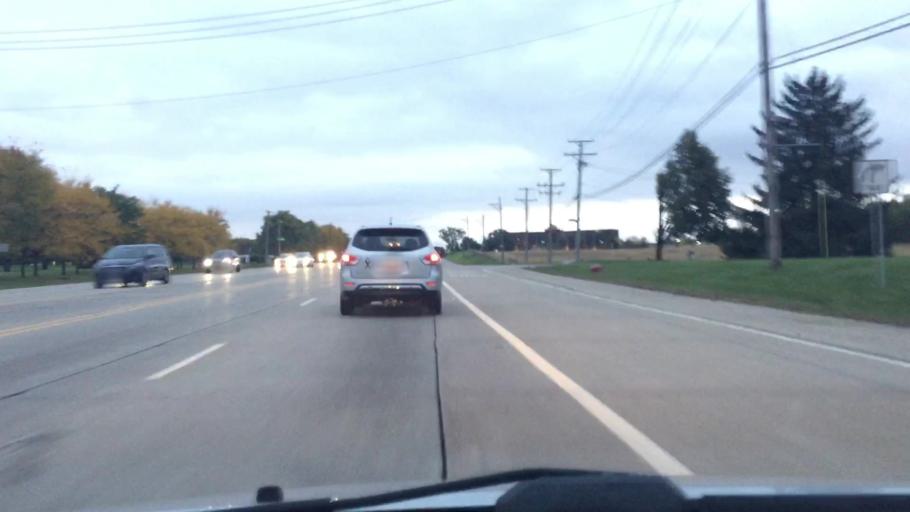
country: US
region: Illinois
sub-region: McHenry County
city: Crystal Lake
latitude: 42.2143
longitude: -88.2865
